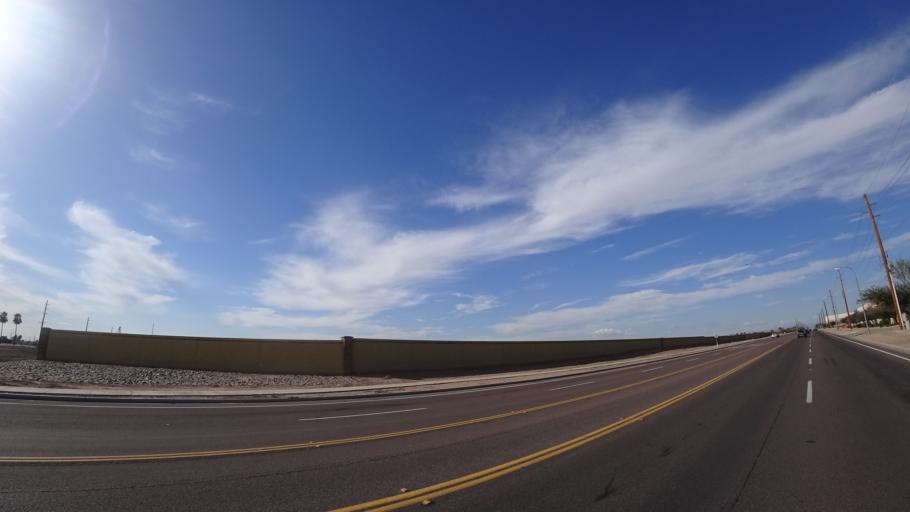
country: US
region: Arizona
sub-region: Maricopa County
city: Tolleson
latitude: 33.4368
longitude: -112.2896
